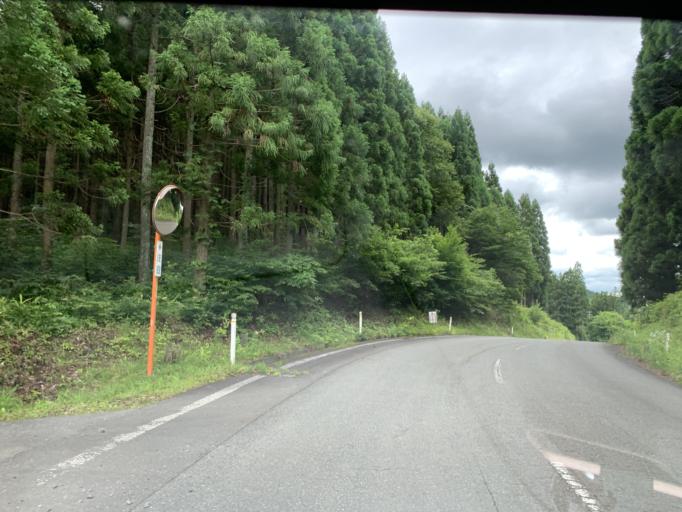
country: JP
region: Iwate
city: Ichinoseki
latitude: 38.8927
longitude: 140.9819
